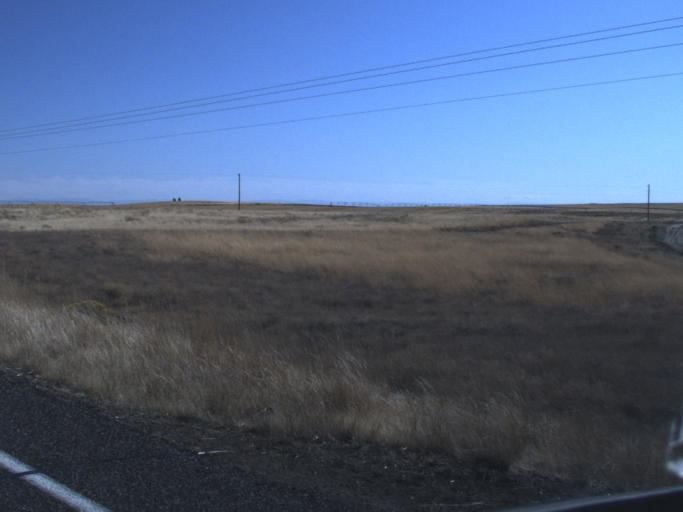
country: US
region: Washington
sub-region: Walla Walla County
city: Burbank
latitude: 46.2976
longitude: -118.7023
